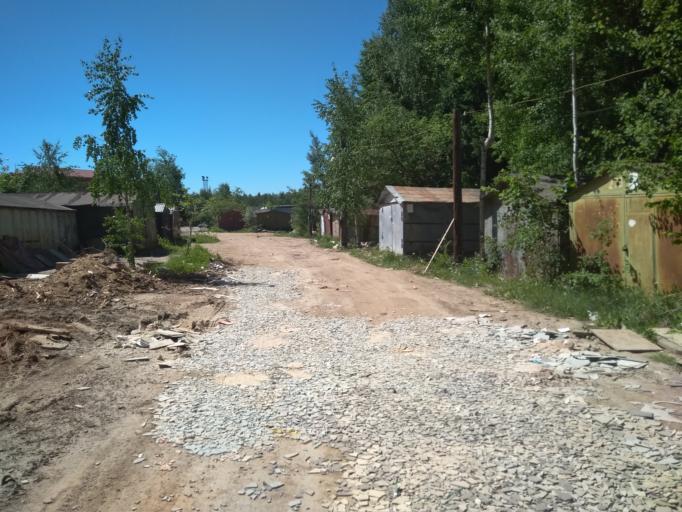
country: RU
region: Moskovskaya
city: Troitsk
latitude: 55.4651
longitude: 37.2828
